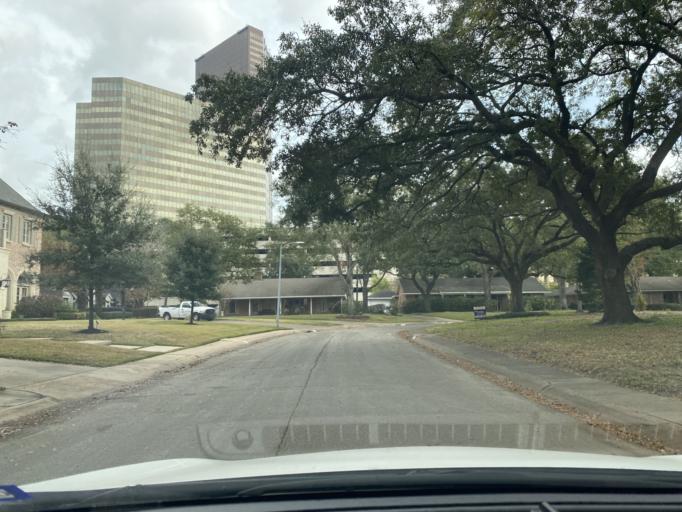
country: US
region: Texas
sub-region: Harris County
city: Hunters Creek Village
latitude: 29.7490
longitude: -95.4756
